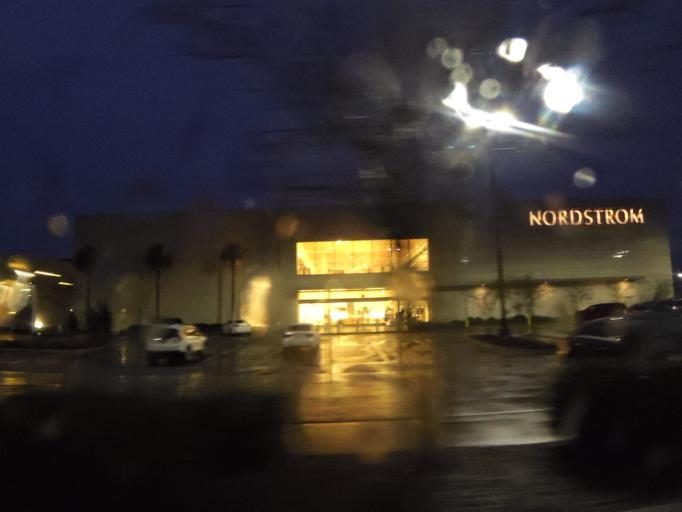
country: US
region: Florida
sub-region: Duval County
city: Jacksonville Beach
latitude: 30.2544
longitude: -81.5268
